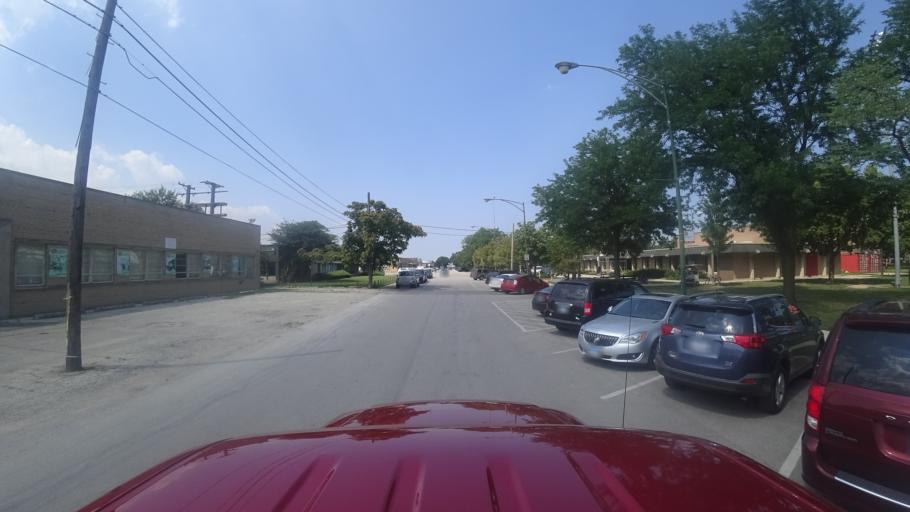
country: US
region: Illinois
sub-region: Cook County
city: Cicero
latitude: 41.8029
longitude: -87.7357
